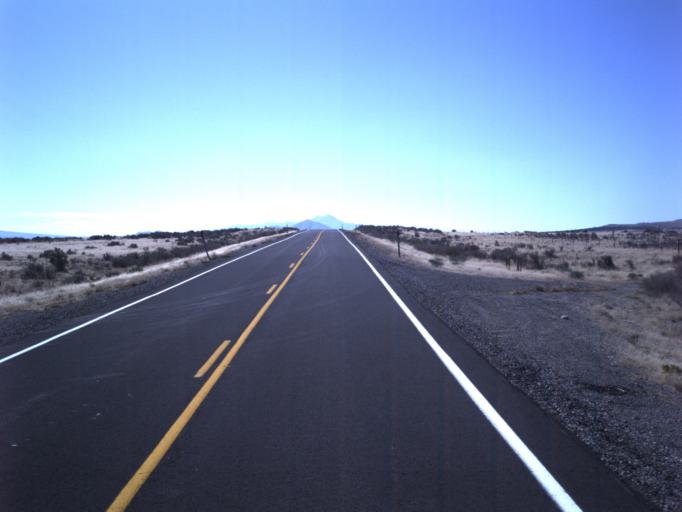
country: US
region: Utah
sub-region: Tooele County
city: Grantsville
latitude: 40.2894
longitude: -112.7423
